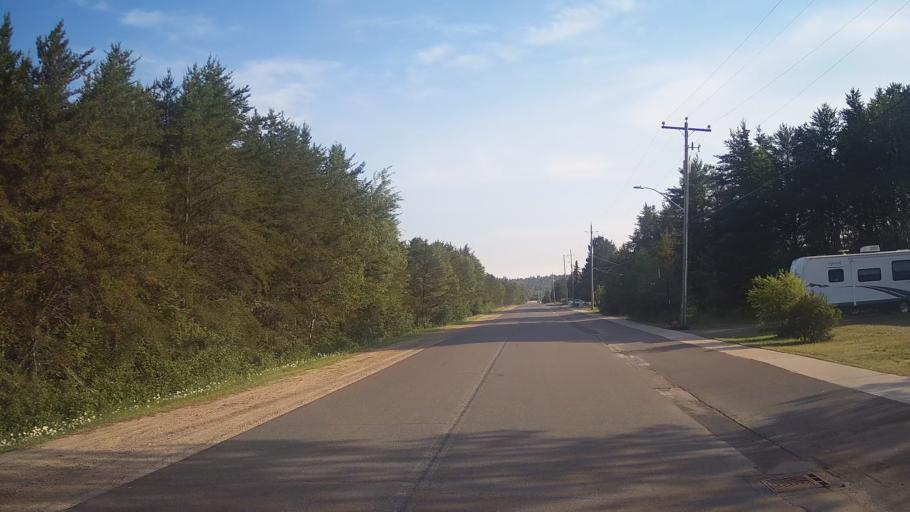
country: CA
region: Ontario
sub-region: Rainy River District
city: Atikokan
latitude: 49.4081
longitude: -91.6664
